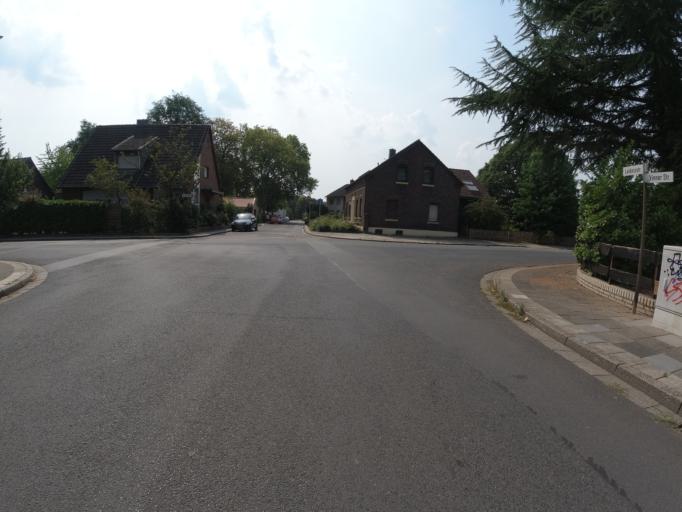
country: DE
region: North Rhine-Westphalia
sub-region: Regierungsbezirk Dusseldorf
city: Moers
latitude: 51.4392
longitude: 6.6302
